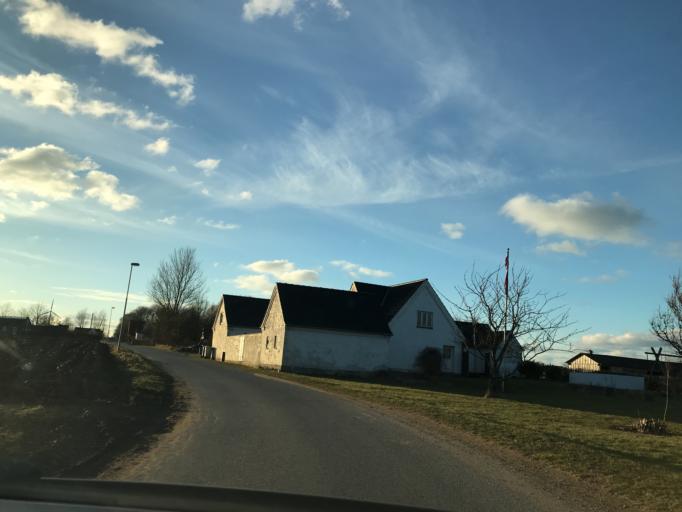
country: DK
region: South Denmark
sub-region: Middelfart Kommune
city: Brenderup
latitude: 55.4633
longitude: 9.9524
